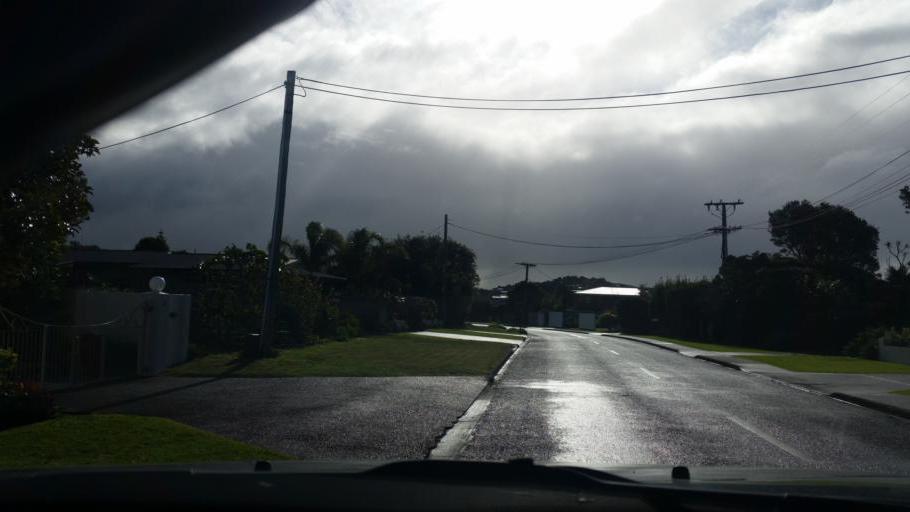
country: NZ
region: Auckland
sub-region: Auckland
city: Wellsford
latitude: -36.0929
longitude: 174.5904
